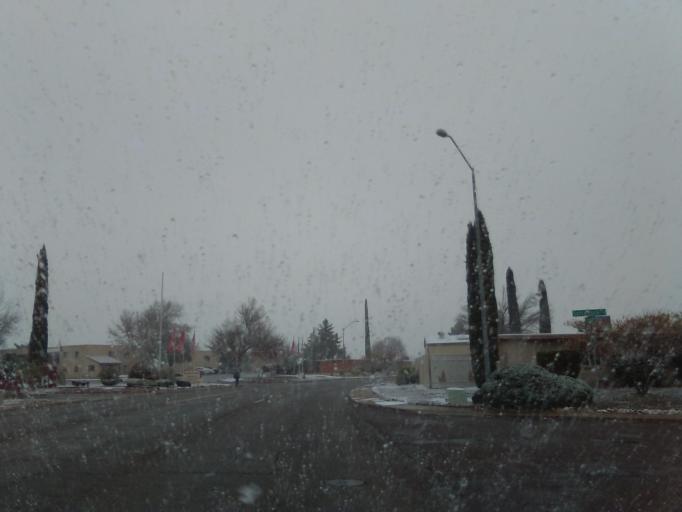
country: US
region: Arizona
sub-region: Cochise County
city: Sierra Vista
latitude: 31.5487
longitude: -110.2786
